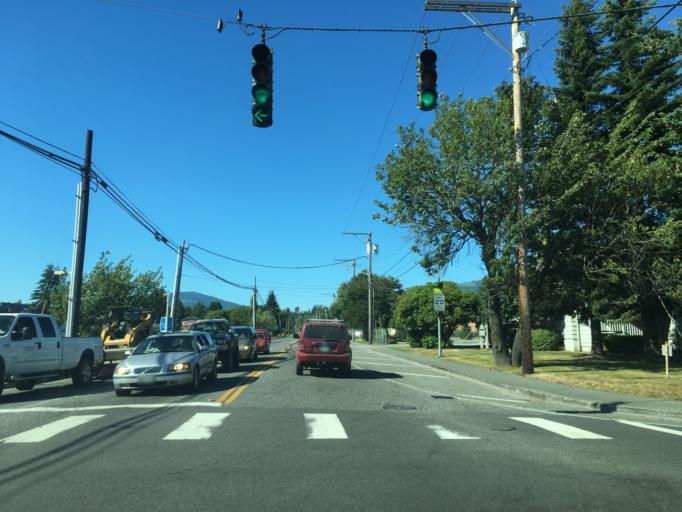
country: US
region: Washington
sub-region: Skagit County
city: Sedro-Woolley
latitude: 48.5106
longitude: -122.2258
